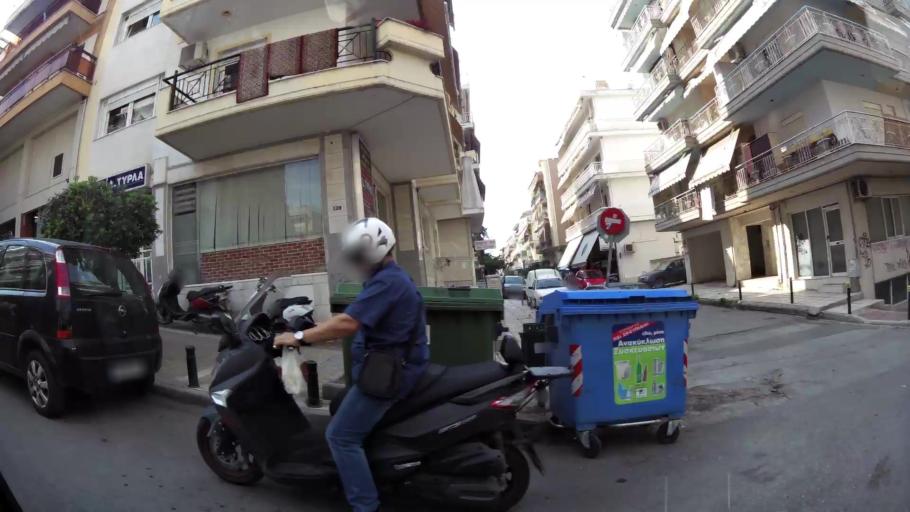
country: GR
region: Central Macedonia
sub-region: Nomos Thessalonikis
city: Sykies
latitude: 40.6533
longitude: 22.9432
